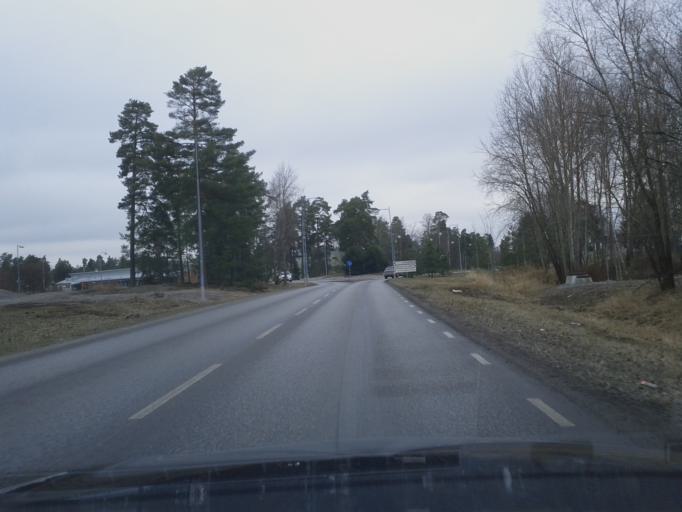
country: SE
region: Stockholm
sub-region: Vallentuna Kommun
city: Vallentuna
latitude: 59.5080
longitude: 18.0645
